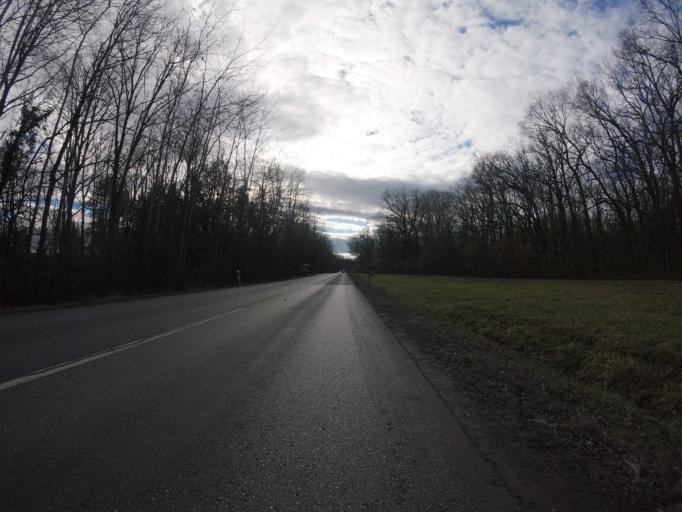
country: HR
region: Zagrebacka
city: Gradici
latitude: 45.6697
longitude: 16.0587
